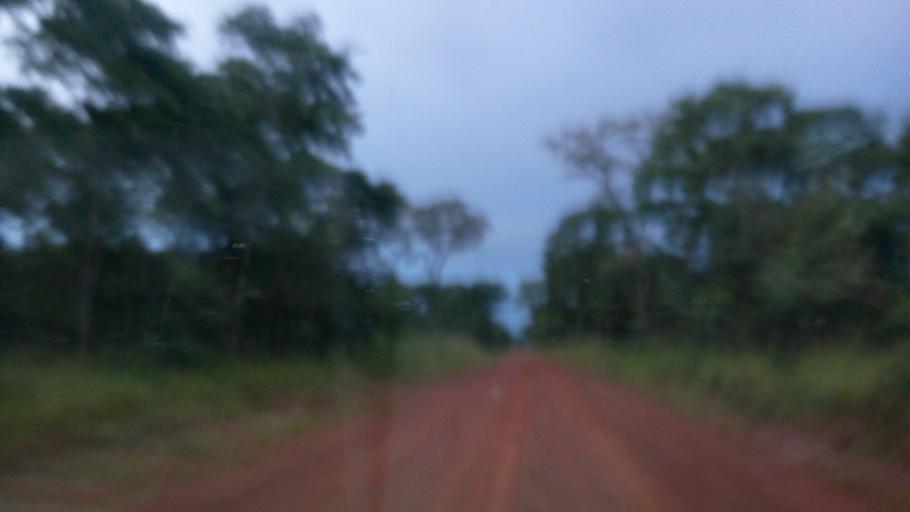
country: ZM
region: Luapula
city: Mwense
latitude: -9.8792
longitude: 28.1055
